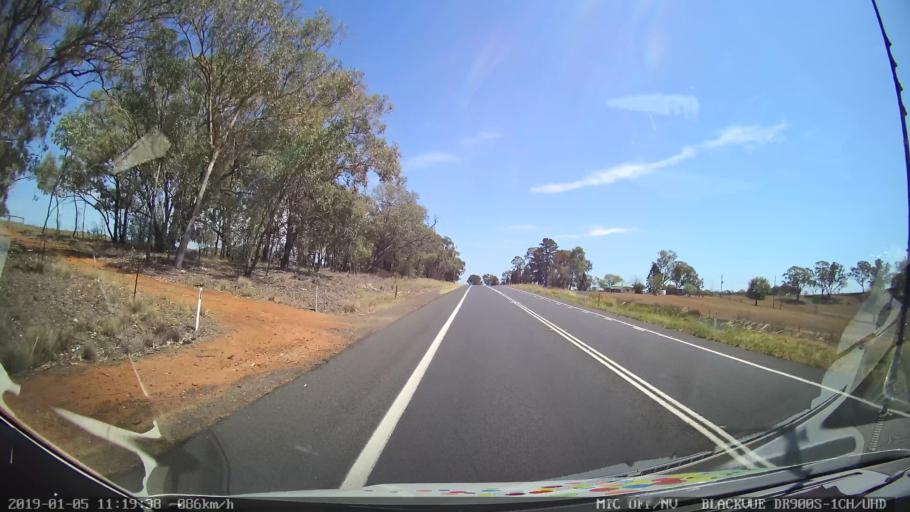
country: AU
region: New South Wales
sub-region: Warrumbungle Shire
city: Coonabarabran
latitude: -31.3015
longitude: 149.2947
